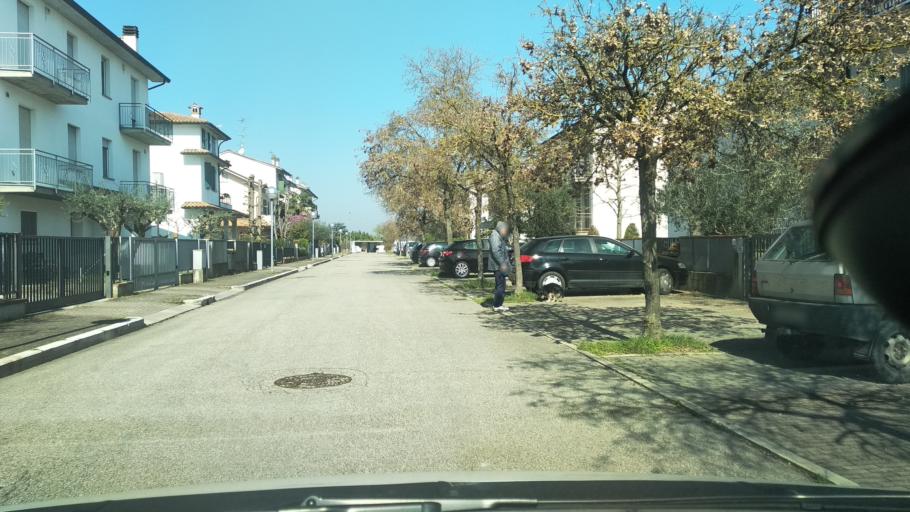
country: IT
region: Emilia-Romagna
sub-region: Provincia di Ravenna
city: Faenza
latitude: 44.2577
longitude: 11.8683
